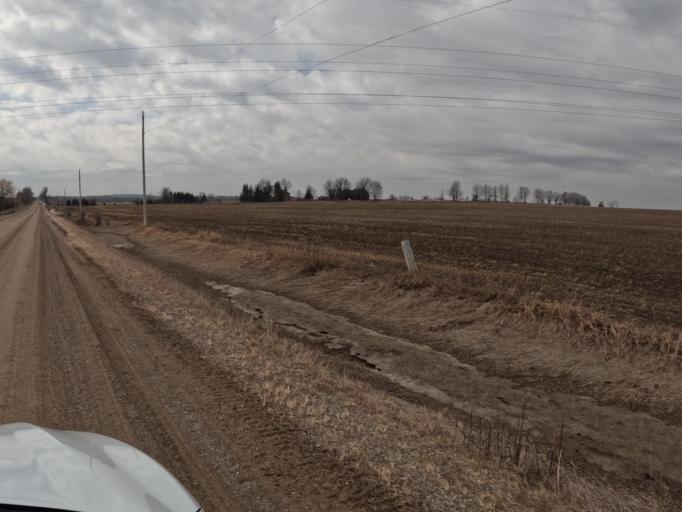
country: CA
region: Ontario
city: Orangeville
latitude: 43.9253
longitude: -80.1867
